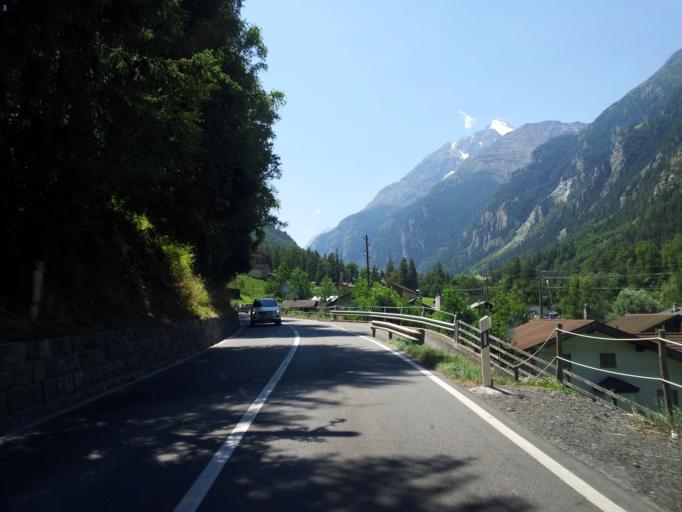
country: CH
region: Valais
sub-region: Visp District
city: Sankt Niklaus
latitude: 46.1877
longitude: 7.8118
